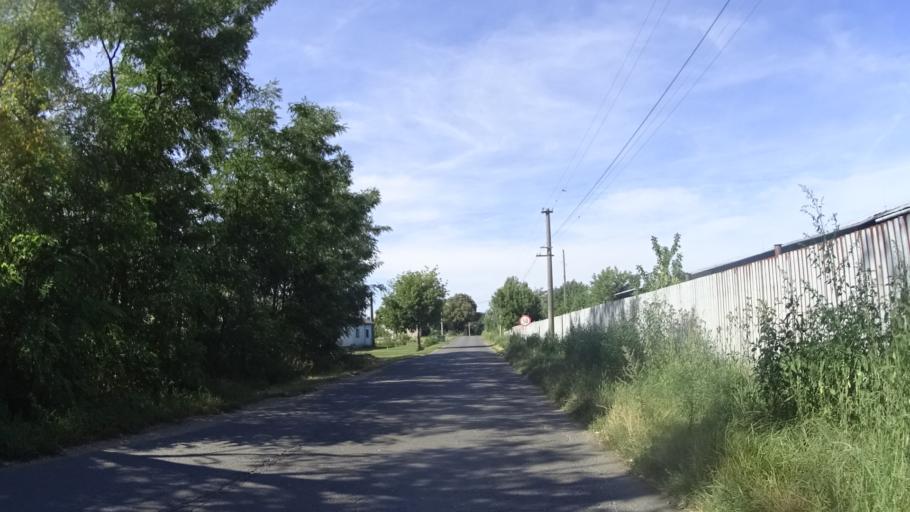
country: AT
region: Lower Austria
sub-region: Politischer Bezirk Ganserndorf
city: Angern an der March
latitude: 48.4117
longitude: 16.8733
